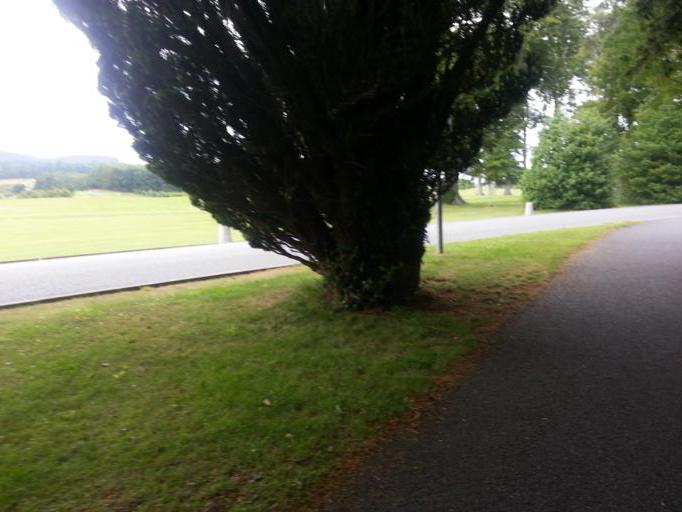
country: IE
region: Leinster
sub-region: Wicklow
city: Enniskerry
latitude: 53.1856
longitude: -6.1865
